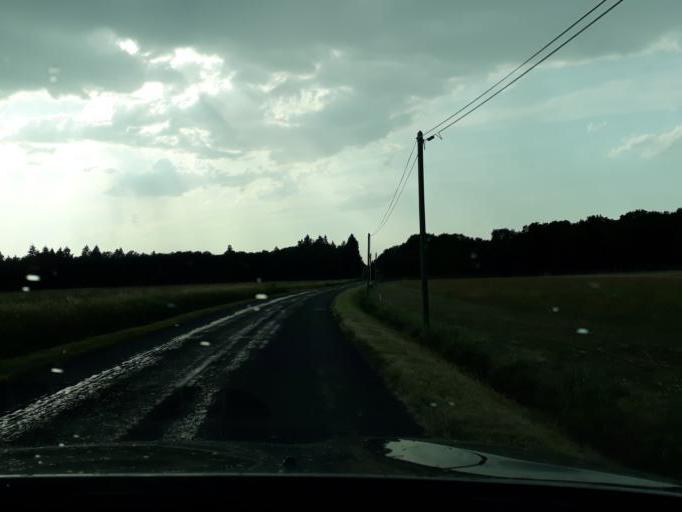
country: FR
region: Centre
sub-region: Departement du Loiret
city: Marcilly-en-Villette
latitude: 47.7604
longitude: 2.0367
